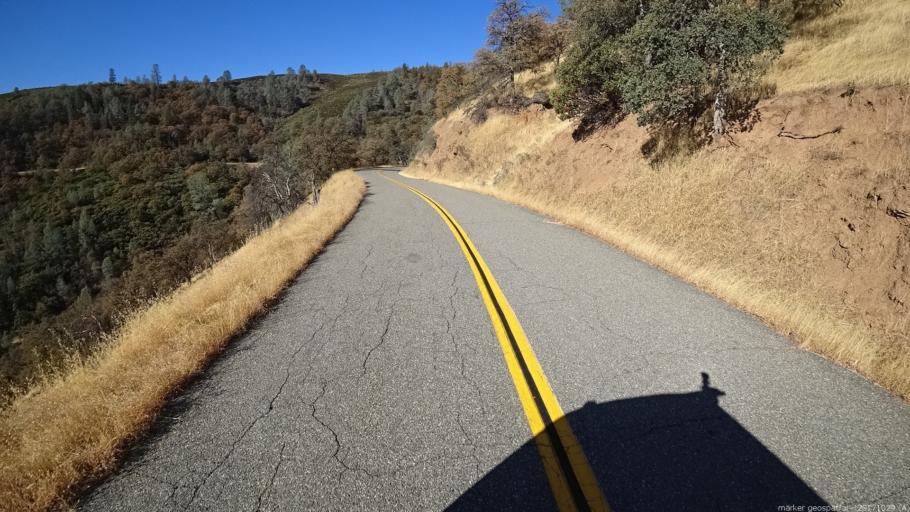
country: US
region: California
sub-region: Trinity County
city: Lewiston
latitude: 40.3770
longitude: -122.8463
